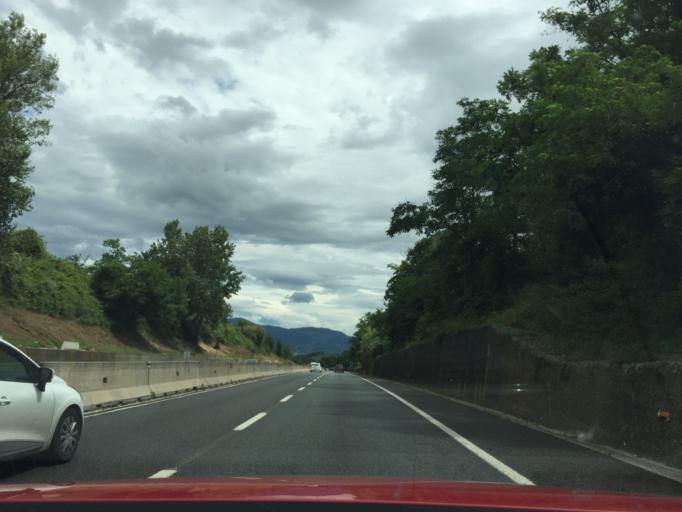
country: IT
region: Tuscany
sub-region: Province of Florence
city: Lastra a Signa
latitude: 43.7413
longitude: 11.1159
